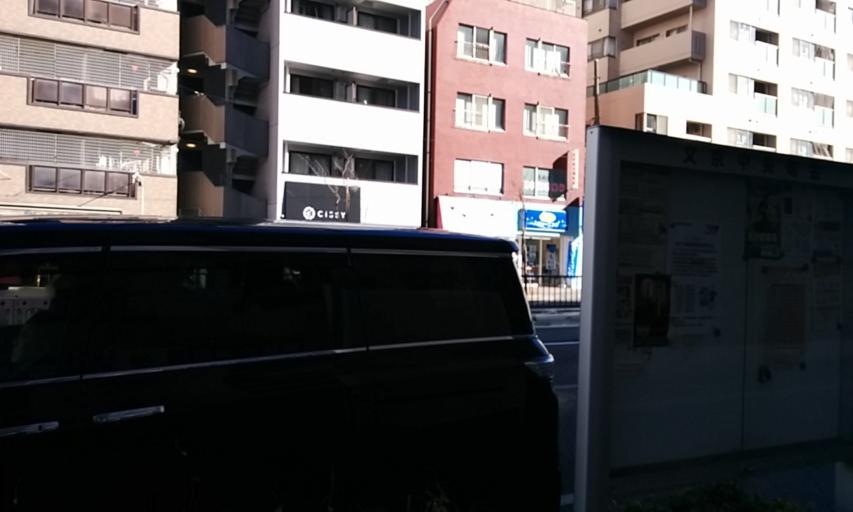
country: JP
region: Tokyo
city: Tokyo
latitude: 35.7160
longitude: 139.7392
